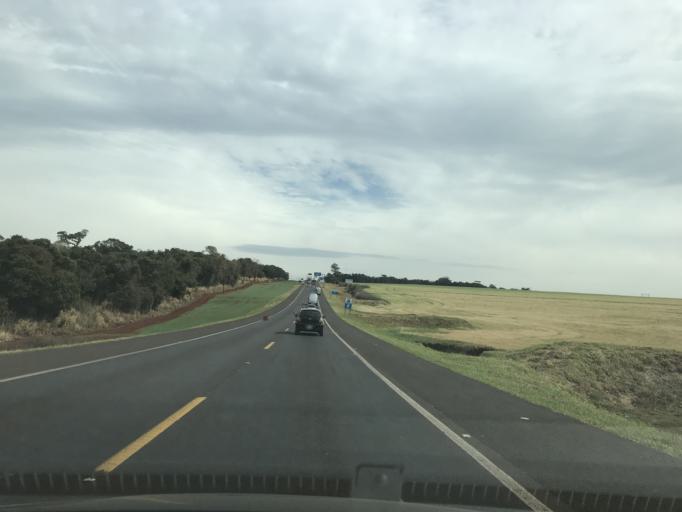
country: BR
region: Parana
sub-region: Cascavel
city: Cascavel
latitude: -25.0799
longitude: -53.7031
